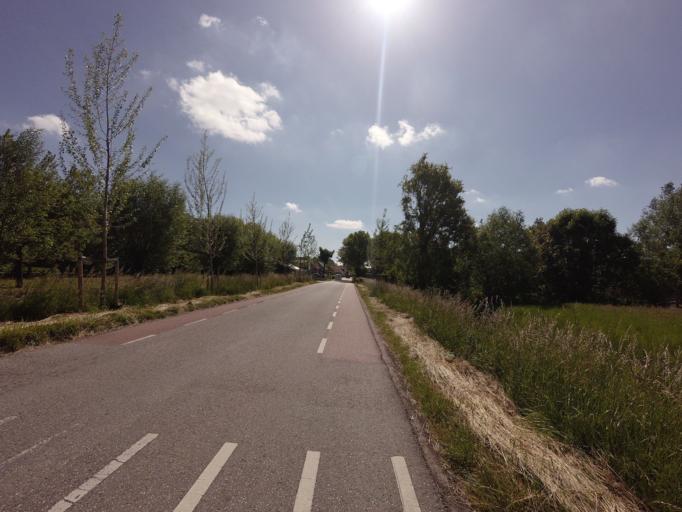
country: NL
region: Utrecht
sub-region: Gemeente IJsselstein
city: IJsselstein
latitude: 52.0470
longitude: 5.0447
